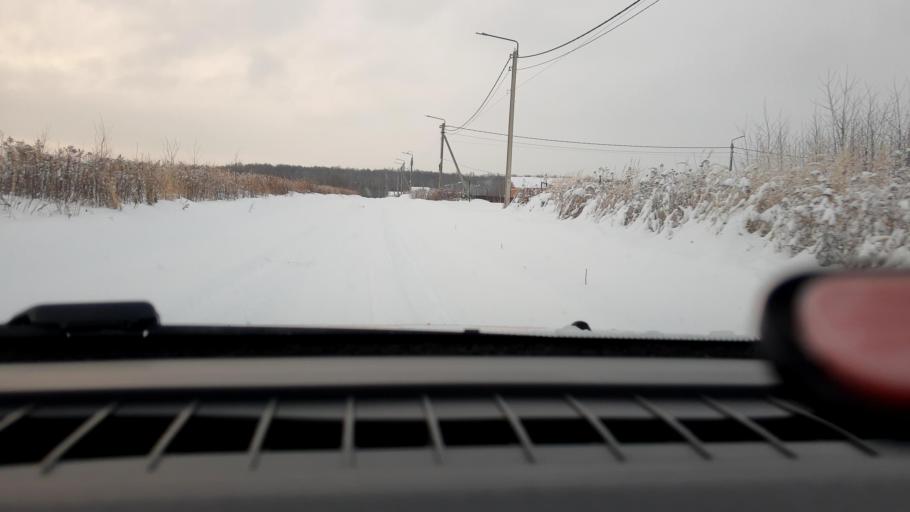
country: RU
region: Nizjnij Novgorod
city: Afonino
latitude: 56.1332
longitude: 43.9873
